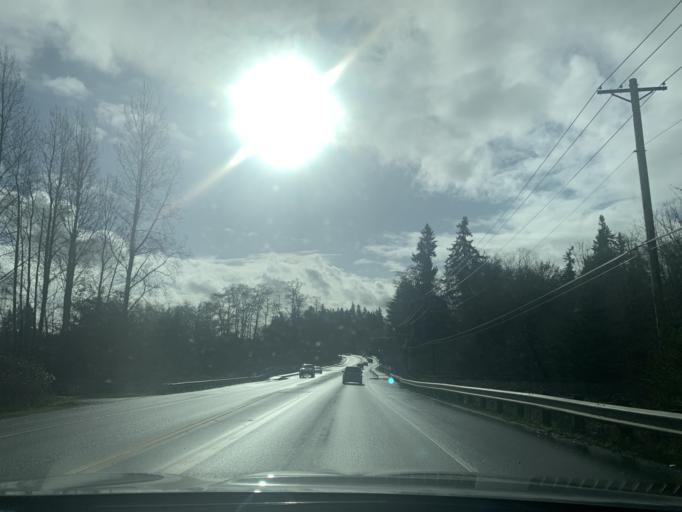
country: US
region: Oregon
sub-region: Washington County
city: Sherwood
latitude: 45.3758
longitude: -122.8568
